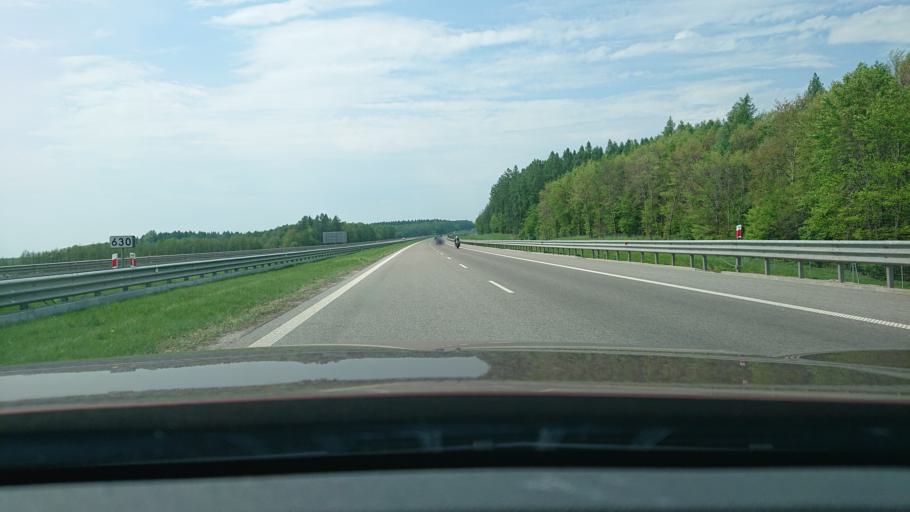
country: PL
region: Subcarpathian Voivodeship
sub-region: Powiat jaroslawski
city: Pawlosiow
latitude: 49.9850
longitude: 22.6189
